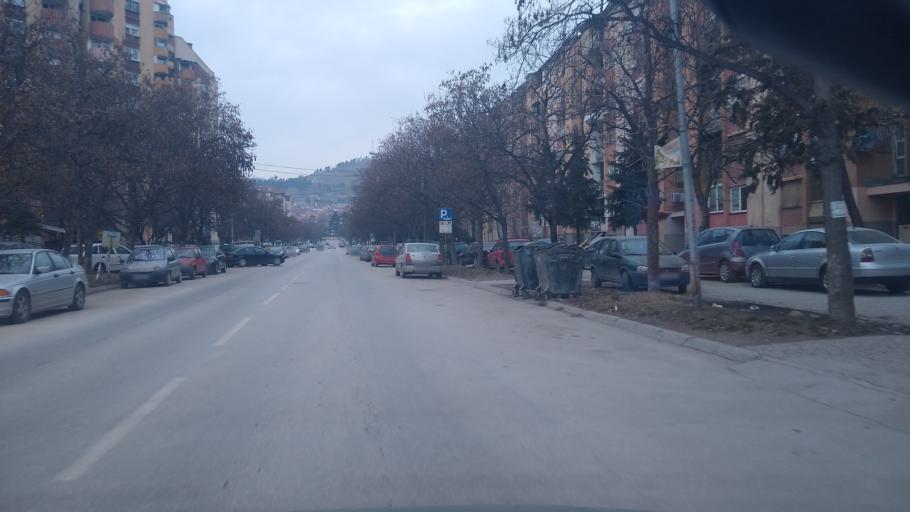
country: MK
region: Bitola
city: Bitola
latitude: 41.0337
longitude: 21.3416
